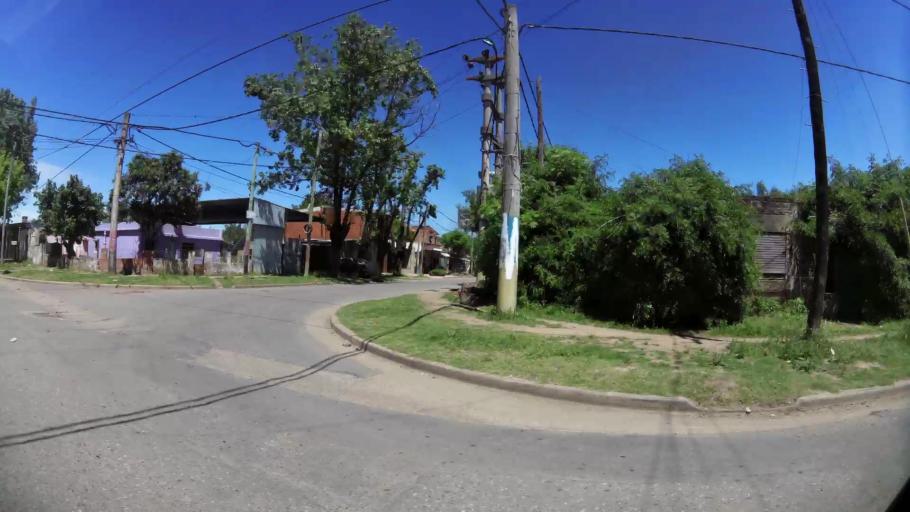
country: AR
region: Santa Fe
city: Perez
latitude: -32.9499
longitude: -60.7192
